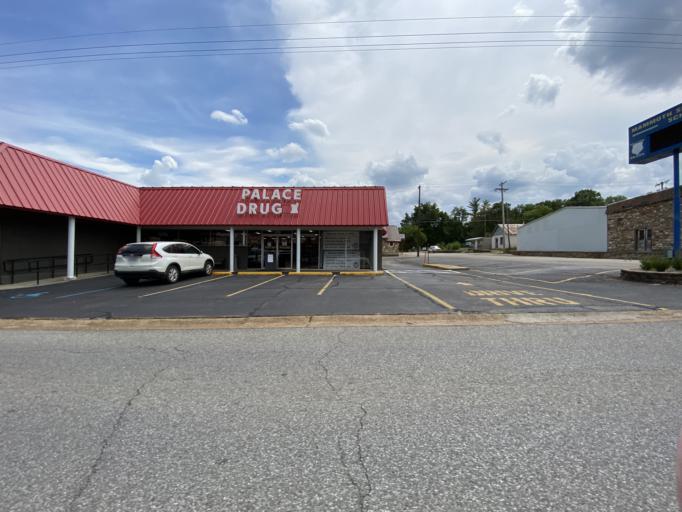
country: US
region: Missouri
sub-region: Oregon County
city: Thayer
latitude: 36.4957
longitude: -91.5402
